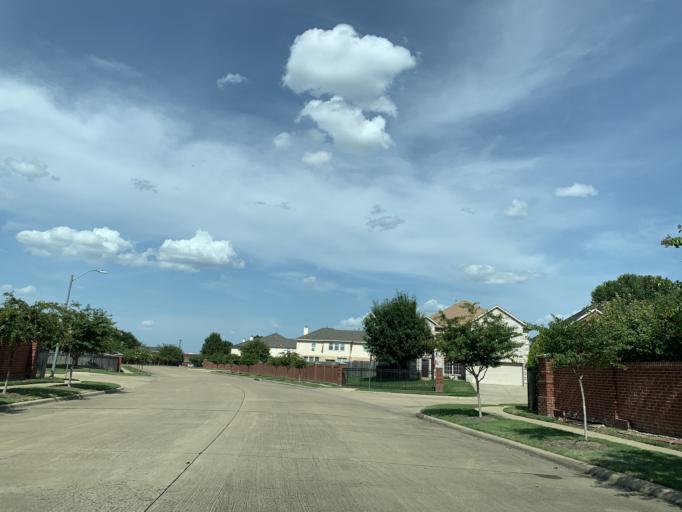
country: US
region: Texas
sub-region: Dallas County
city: Cedar Hill
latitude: 32.6490
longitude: -97.0097
